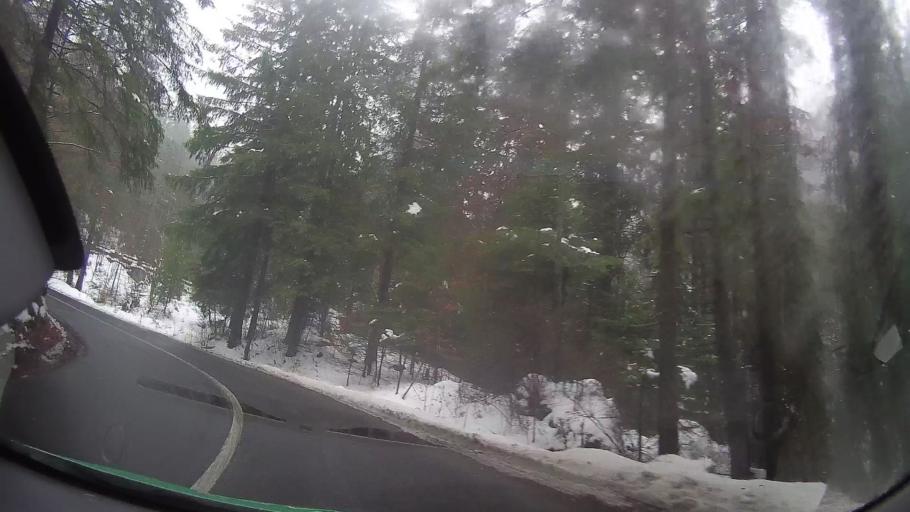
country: RO
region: Neamt
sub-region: Comuna Bicaz Chei
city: Bicaz Chei
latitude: 46.8072
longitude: 25.8114
